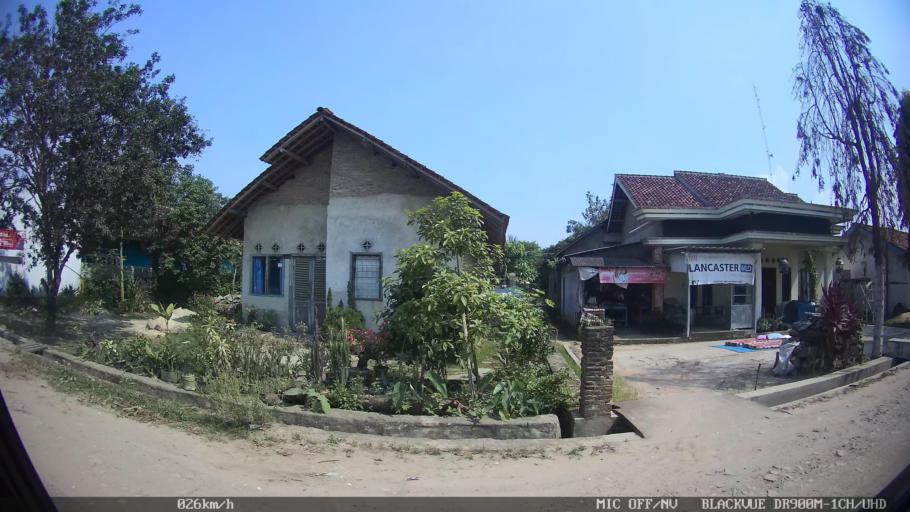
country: ID
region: Lampung
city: Natar
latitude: -5.3064
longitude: 105.2236
